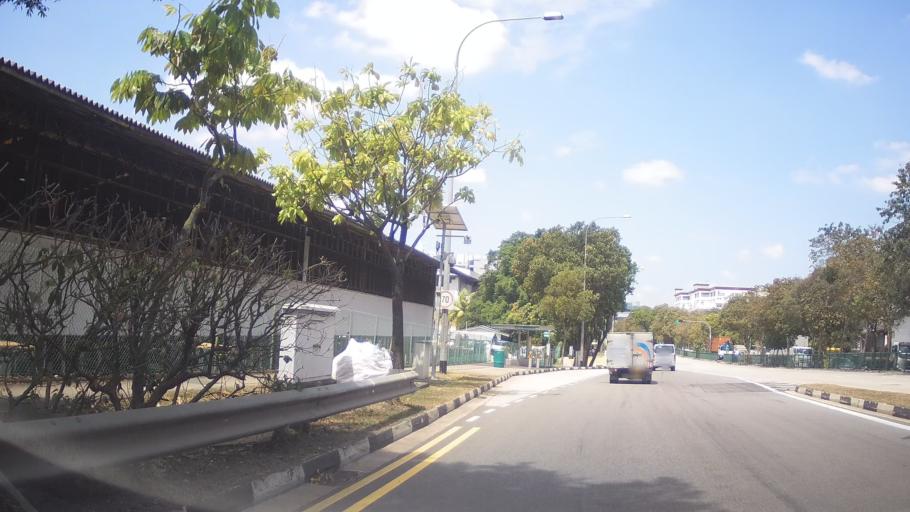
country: SG
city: Singapore
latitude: 1.3140
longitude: 103.7088
